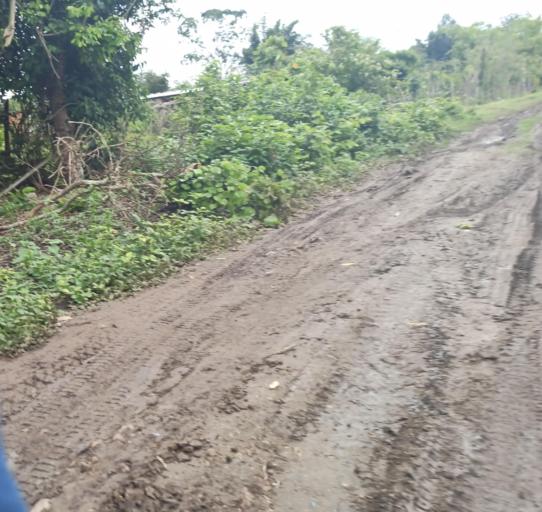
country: MX
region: Puebla
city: Espinal
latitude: 20.3252
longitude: -97.4194
